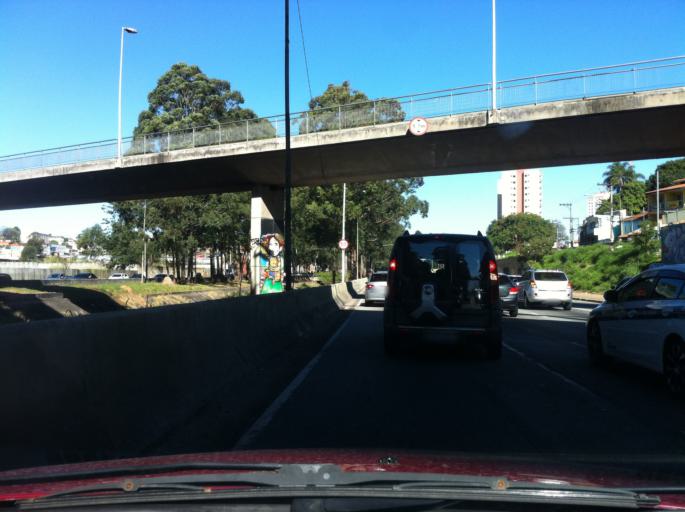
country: BR
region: Sao Paulo
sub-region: Ferraz De Vasconcelos
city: Ferraz de Vasconcelos
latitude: -23.5418
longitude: -46.4490
